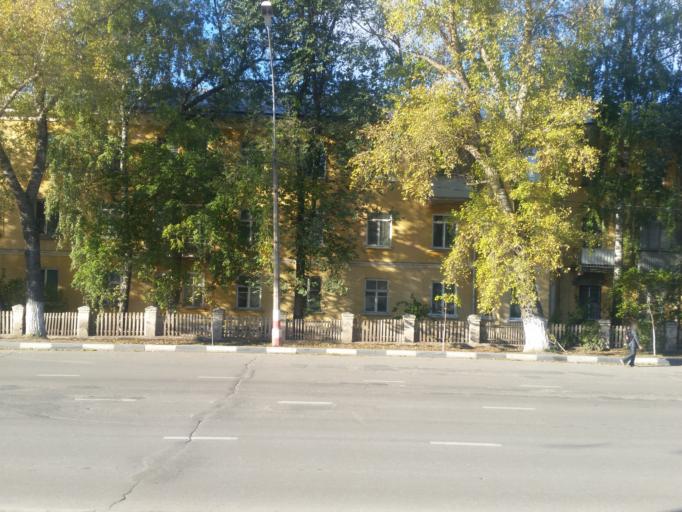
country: RU
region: Ulyanovsk
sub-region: Ulyanovskiy Rayon
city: Ulyanovsk
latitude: 54.3367
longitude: 48.3822
